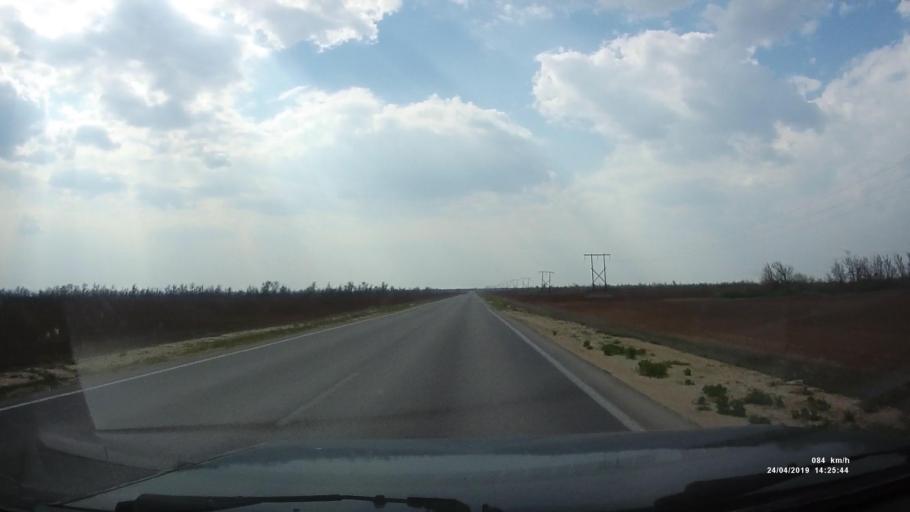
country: RU
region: Kalmykiya
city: Arshan'
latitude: 46.3315
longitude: 44.0763
